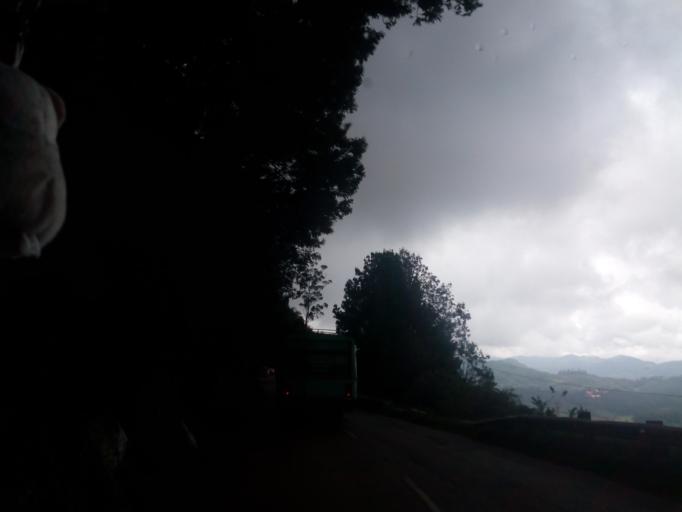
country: IN
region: Tamil Nadu
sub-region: Nilgiri
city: Ooty
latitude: 11.3895
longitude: 76.7205
